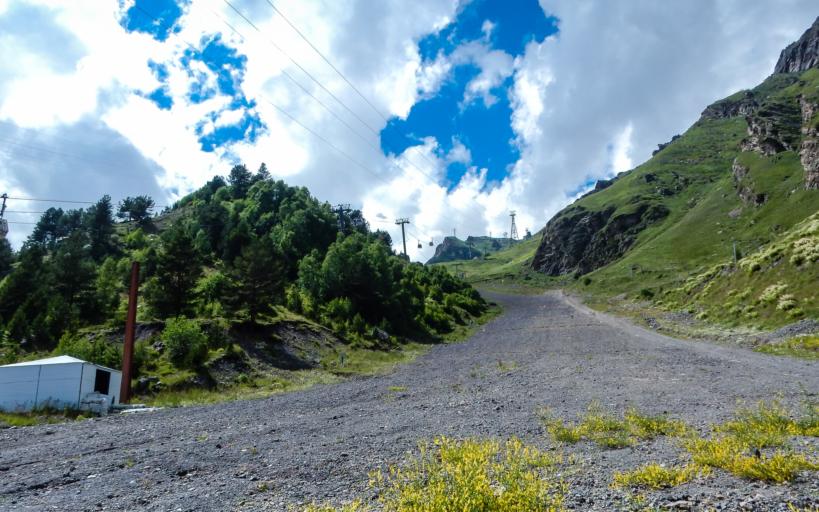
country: RU
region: Kabardino-Balkariya
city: Terskol
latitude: 43.2670
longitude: 42.4775
